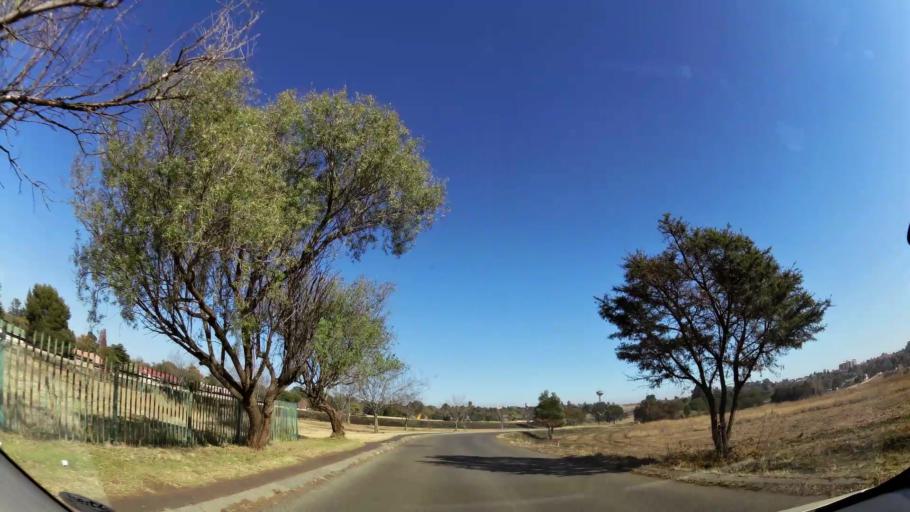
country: ZA
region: Mpumalanga
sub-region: Nkangala District Municipality
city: Witbank
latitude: -25.8921
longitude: 29.2419
